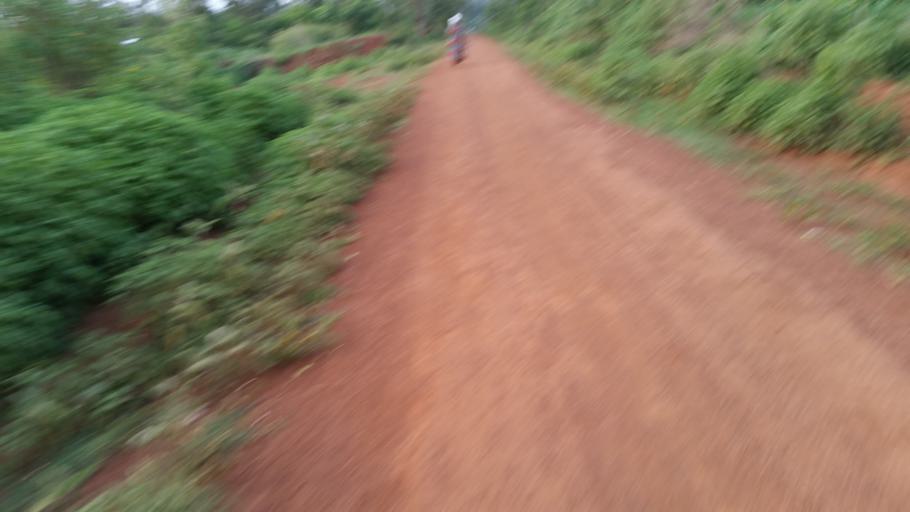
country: UG
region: Eastern Region
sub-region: Busia District
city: Busia
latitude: 0.5415
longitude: 34.0431
